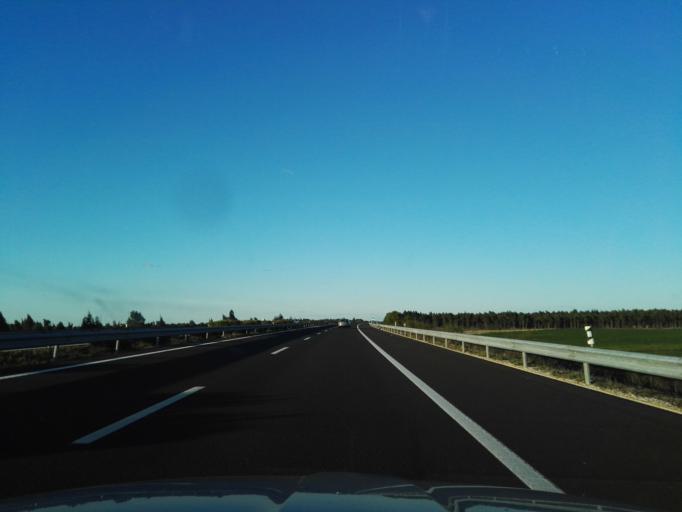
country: PT
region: Santarem
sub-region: Benavente
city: Poceirao
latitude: 38.7570
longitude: -8.6841
